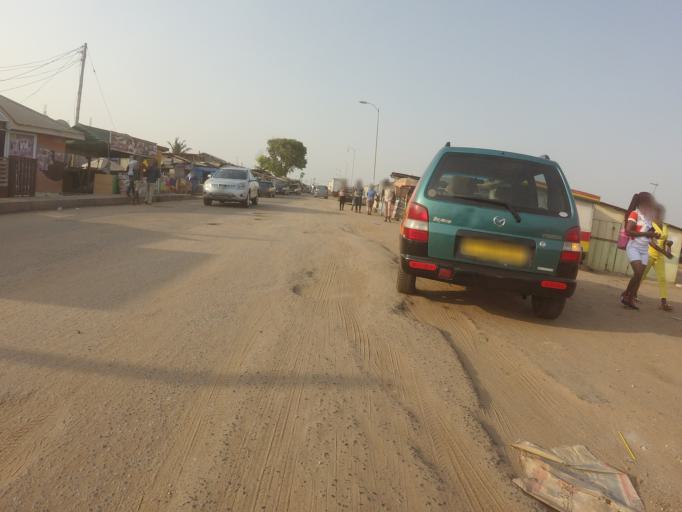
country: GH
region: Greater Accra
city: Nungua
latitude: 5.6119
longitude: -0.0463
